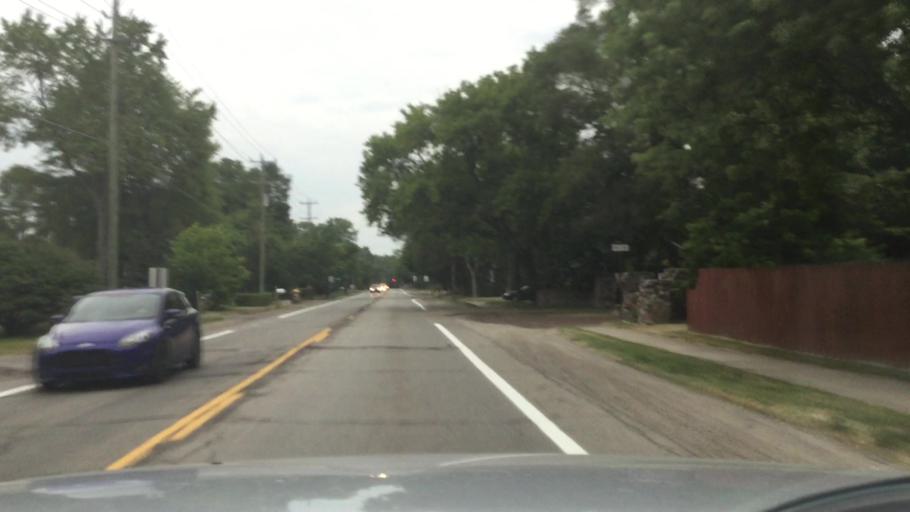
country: US
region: Michigan
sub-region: Oakland County
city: Waterford
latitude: 42.6759
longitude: -83.4315
